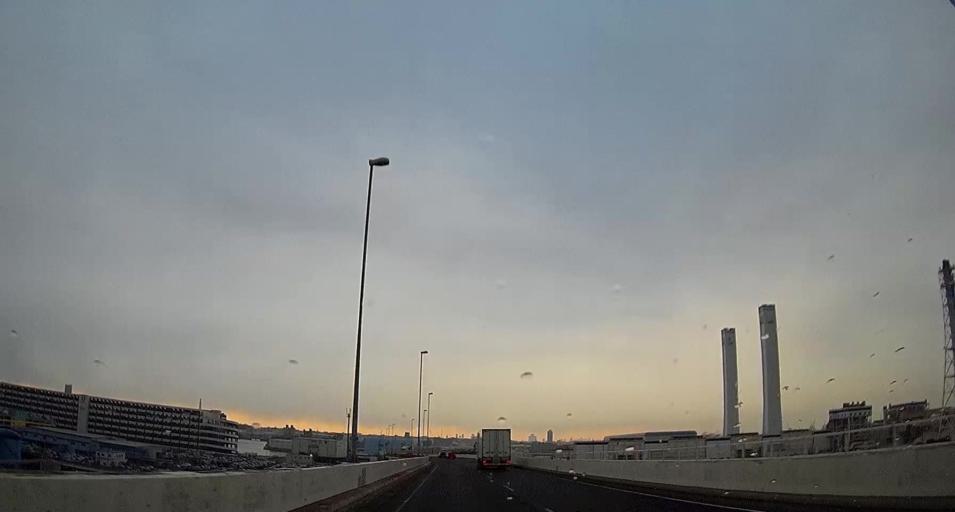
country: JP
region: Kanagawa
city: Yokohama
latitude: 35.4697
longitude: 139.6764
